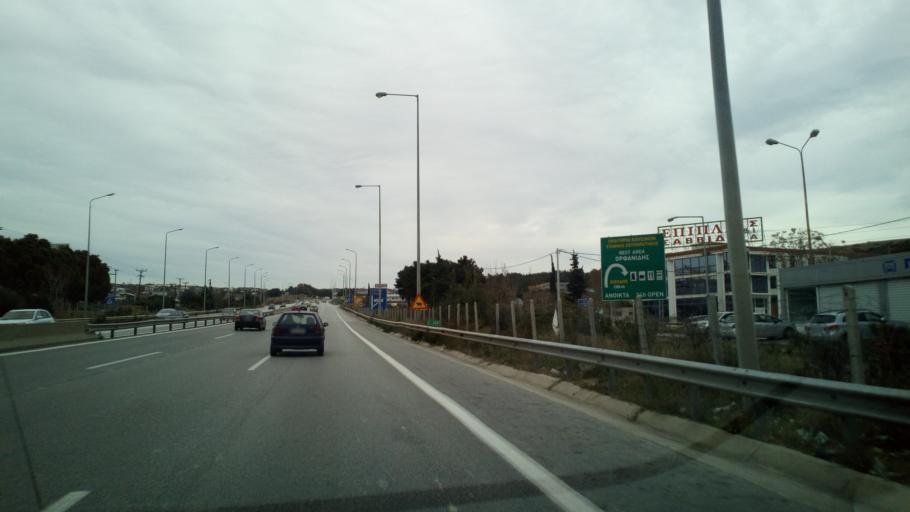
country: GR
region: Central Macedonia
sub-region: Nomos Thessalonikis
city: Efkarpia
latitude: 40.7074
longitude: 22.9543
